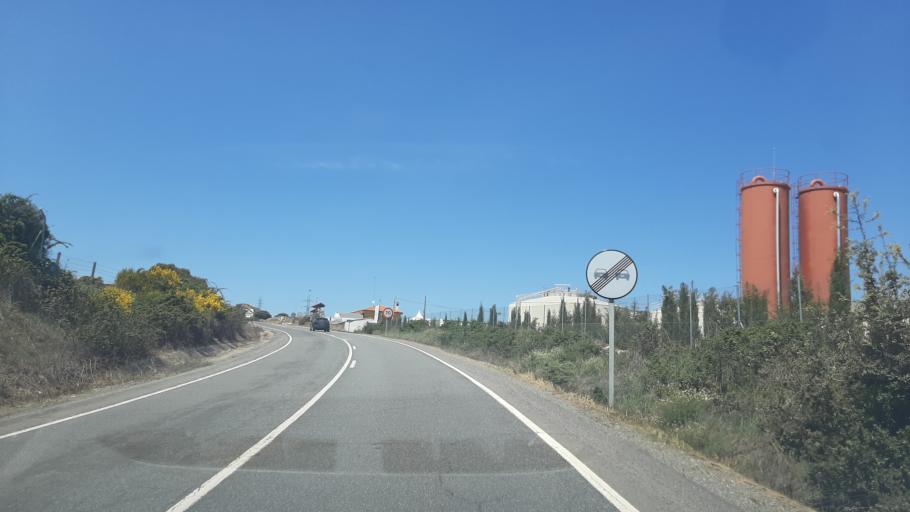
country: ES
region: Castille and Leon
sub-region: Provincia de Salamanca
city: Guijo de Avila
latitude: 40.5555
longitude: -5.6411
